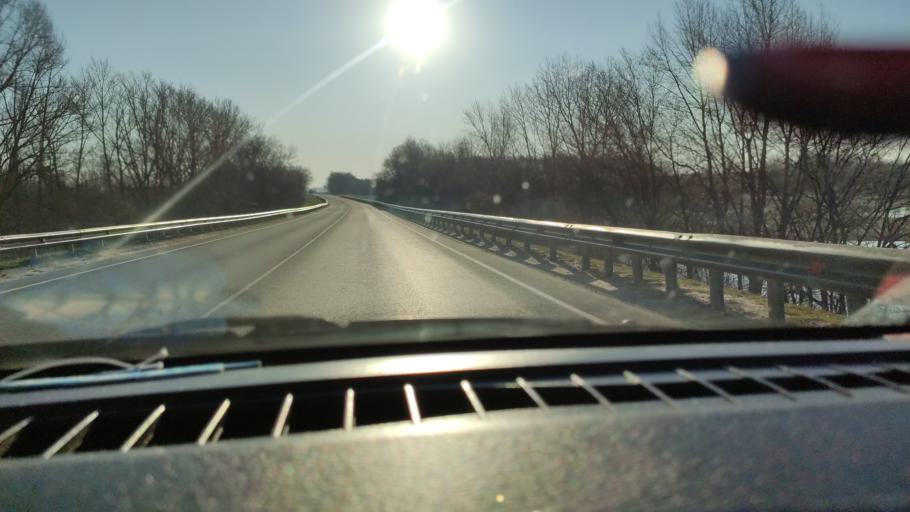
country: RU
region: Saratov
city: Tersa
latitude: 52.0848
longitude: 47.5929
